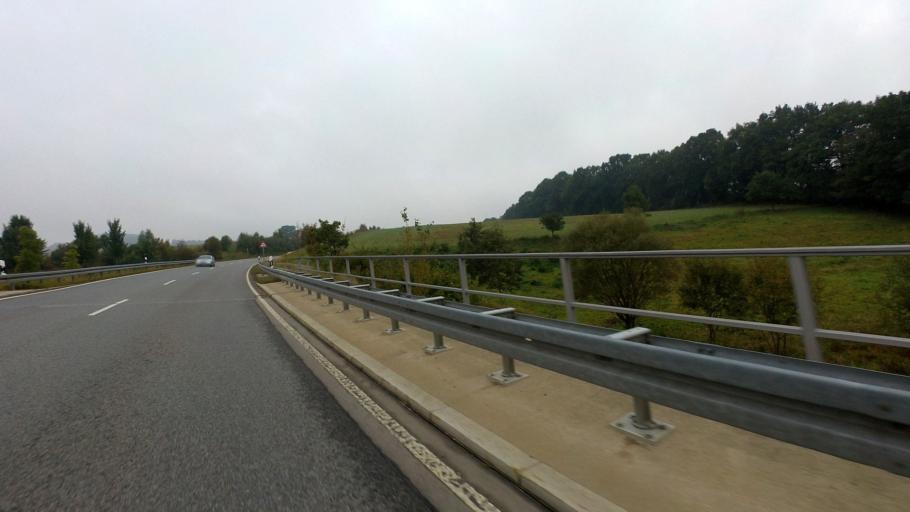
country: DE
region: Saxony
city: Neustadt in Sachsen
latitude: 51.0379
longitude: 14.2149
